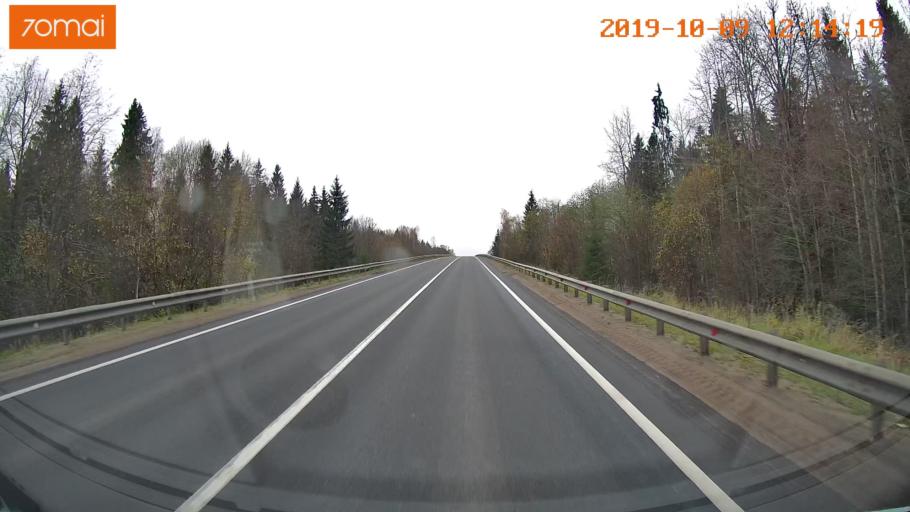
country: RU
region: Jaroslavl
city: Prechistoye
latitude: 58.4976
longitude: 40.3382
